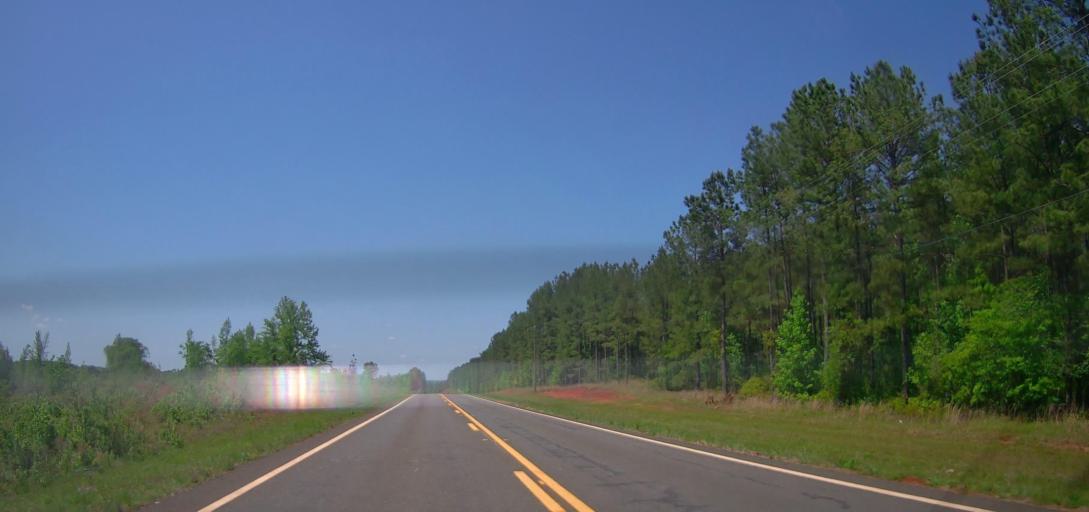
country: US
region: Georgia
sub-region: Jasper County
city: Monticello
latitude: 33.2567
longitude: -83.5688
